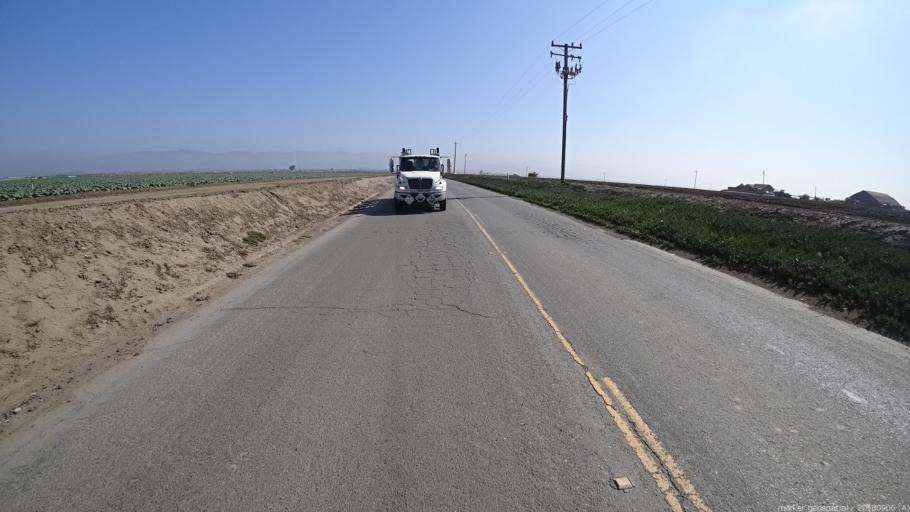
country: US
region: California
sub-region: Monterey County
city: Chualar
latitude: 36.5534
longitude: -121.5391
